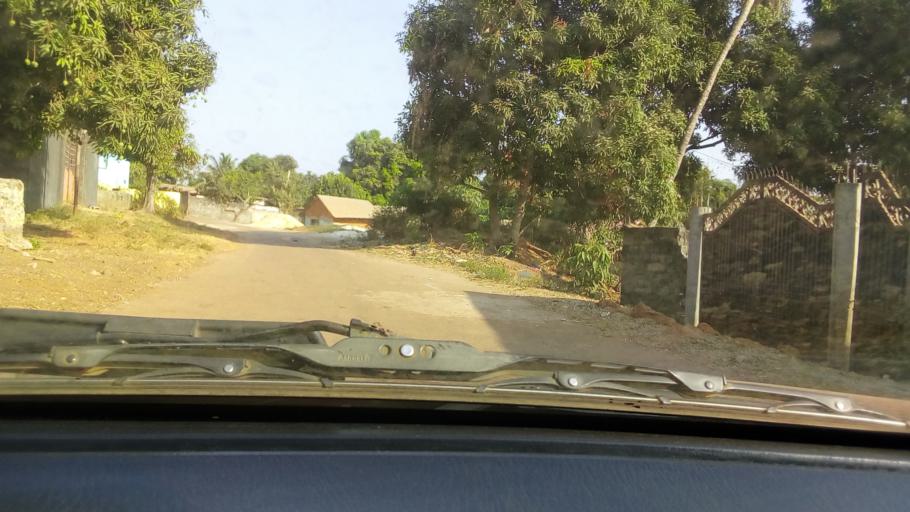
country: GN
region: Kindia
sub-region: Prefecture de Dubreka
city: Dubreka
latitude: 9.7881
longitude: -13.5272
